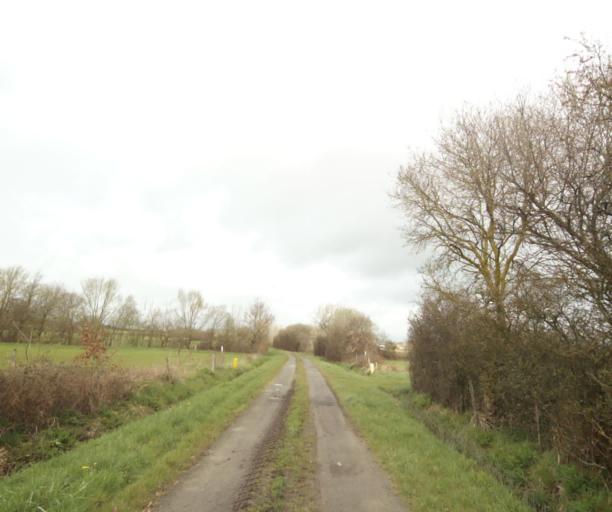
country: FR
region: Pays de la Loire
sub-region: Departement de la Loire-Atlantique
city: Bouvron
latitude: 47.4310
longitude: -1.8923
